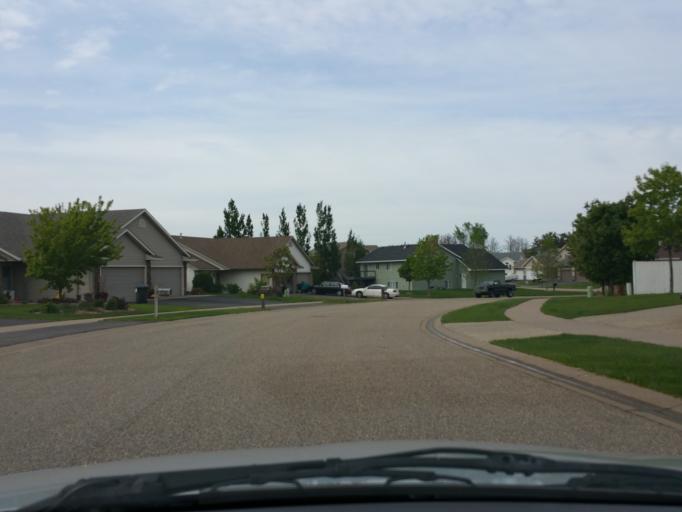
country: US
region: Wisconsin
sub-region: Saint Croix County
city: Hudson
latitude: 44.9534
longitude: -92.6937
